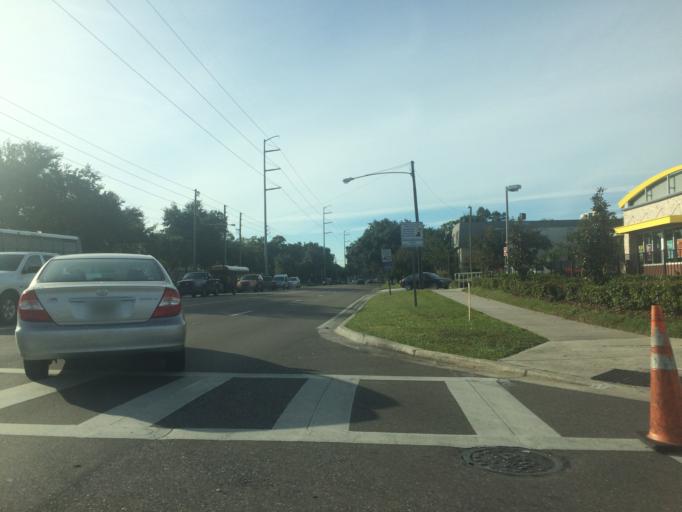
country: US
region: Florida
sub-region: Pinellas County
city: South Highpoint
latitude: 27.9421
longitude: -82.7462
